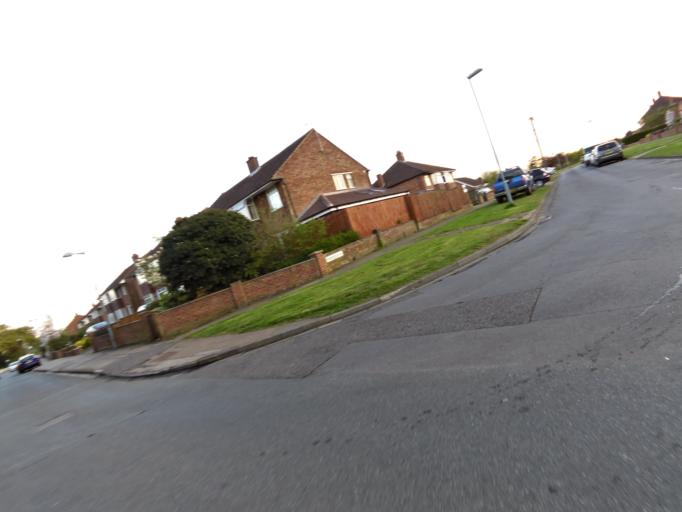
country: GB
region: England
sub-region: Suffolk
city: Kesgrave
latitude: 52.0698
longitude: 1.1986
